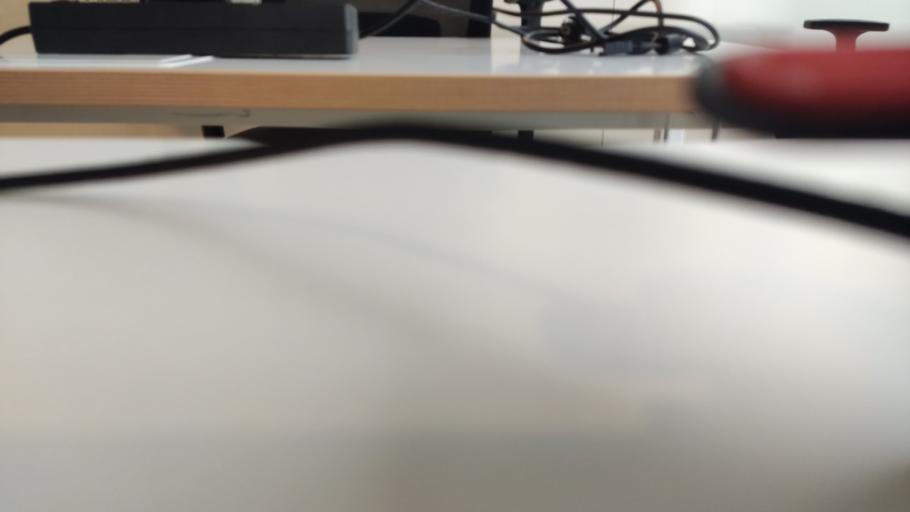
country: RU
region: Moskovskaya
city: Rogachevo
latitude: 56.4270
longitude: 37.1036
